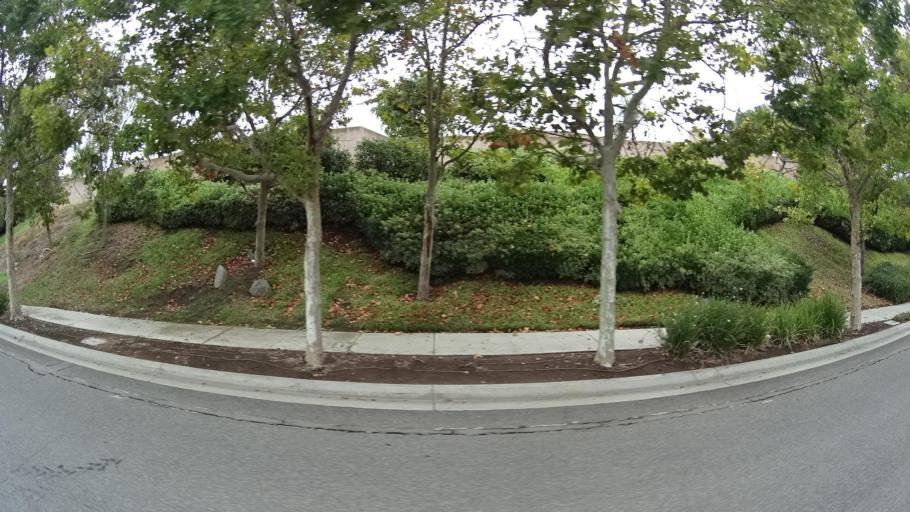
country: US
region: California
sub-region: San Diego County
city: Escondido
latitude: 33.0723
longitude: -117.0772
